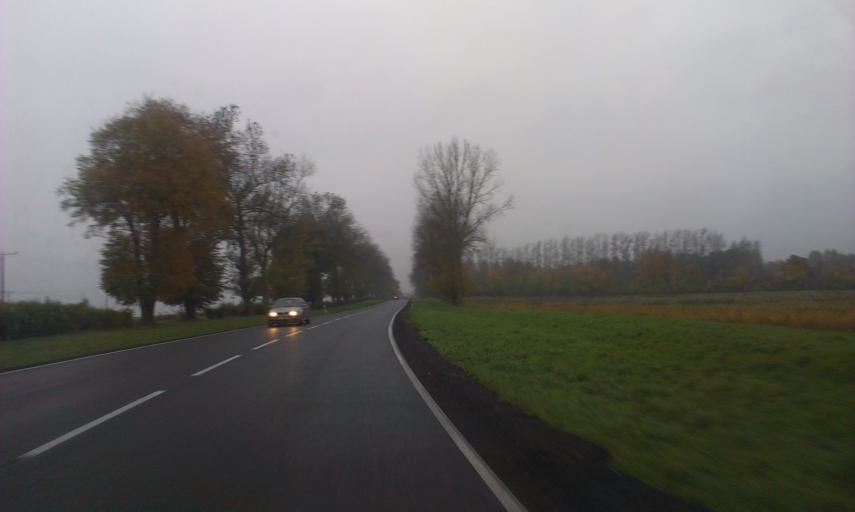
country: PL
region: West Pomeranian Voivodeship
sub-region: Powiat koszalinski
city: Sianow
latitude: 54.1451
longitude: 16.2501
